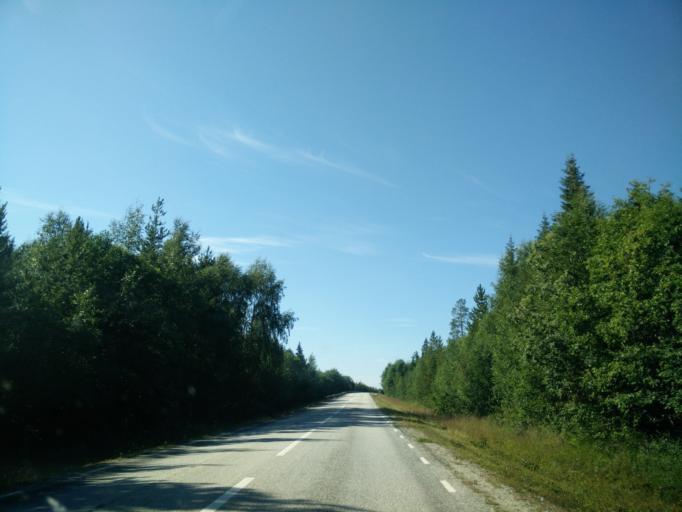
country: SE
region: Jaemtland
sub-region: Are Kommun
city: Jarpen
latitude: 62.7999
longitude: 13.5704
